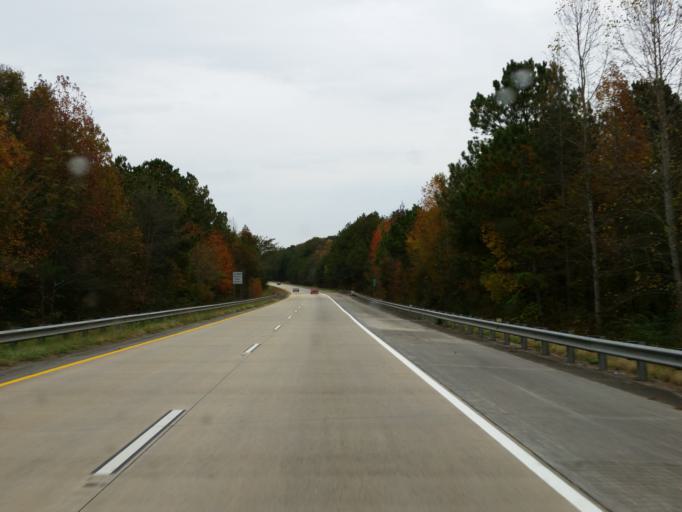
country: US
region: Georgia
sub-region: Cherokee County
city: Ball Ground
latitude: 34.3442
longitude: -84.3902
